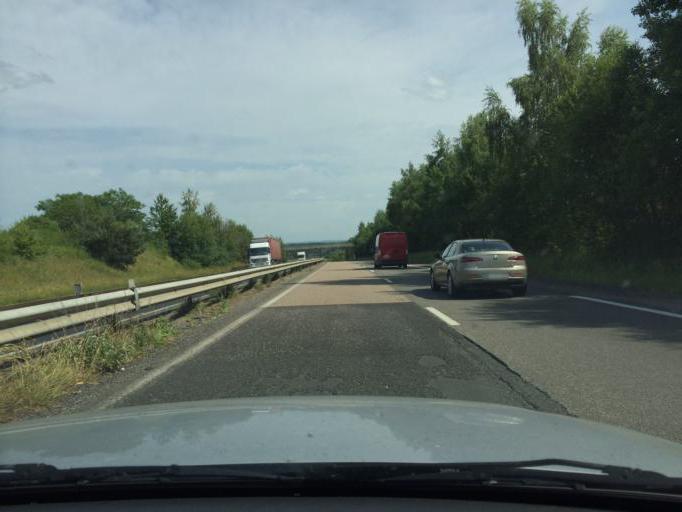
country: FR
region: Lorraine
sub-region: Departement de Meurthe-et-Moselle
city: Domgermain
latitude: 48.6576
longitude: 5.8394
